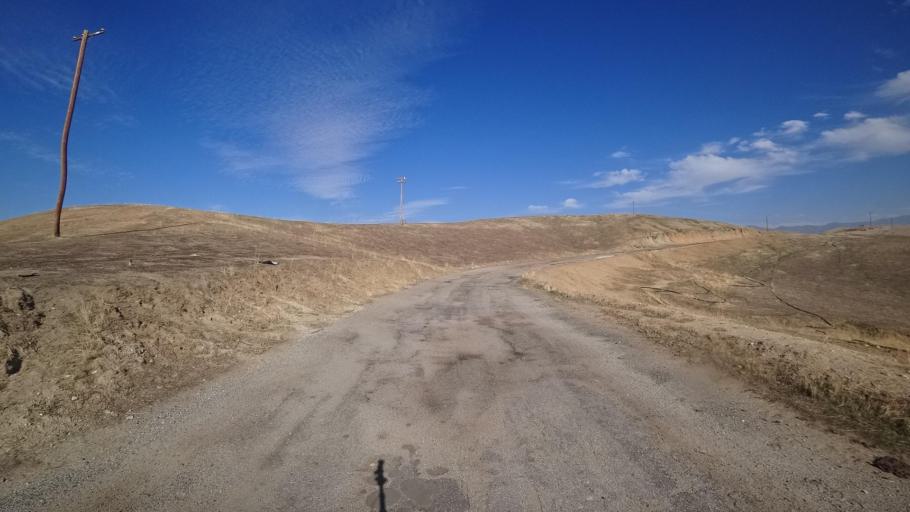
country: US
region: California
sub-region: Kern County
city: Oildale
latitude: 35.4967
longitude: -118.8721
